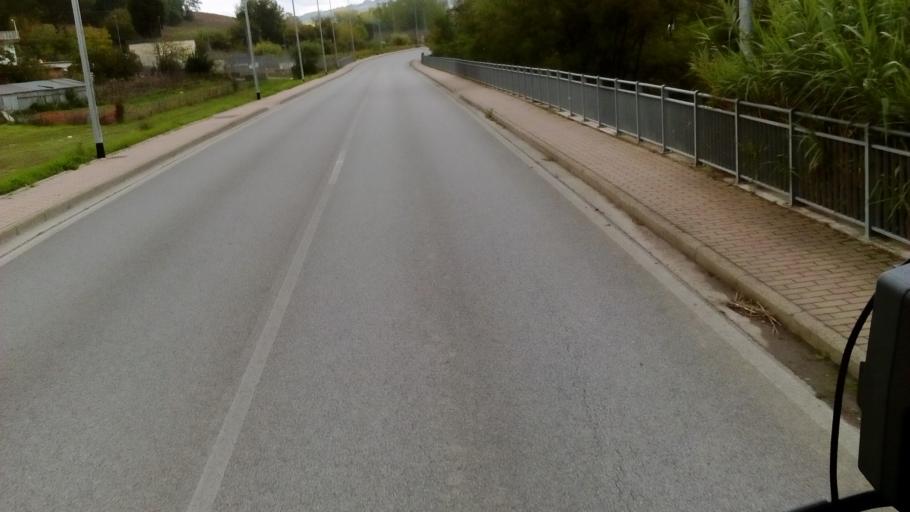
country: IT
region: Tuscany
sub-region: Province of Florence
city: Montespertoli
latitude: 43.6638
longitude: 11.0831
